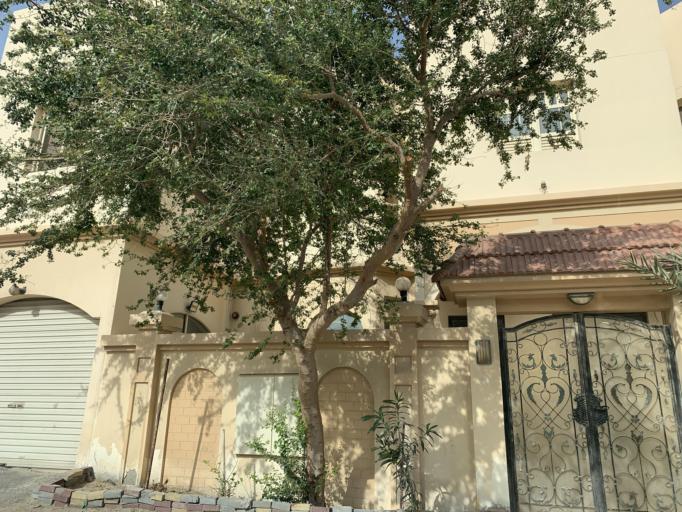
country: BH
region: Northern
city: Madinat `Isa
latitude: 26.1803
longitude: 50.5627
